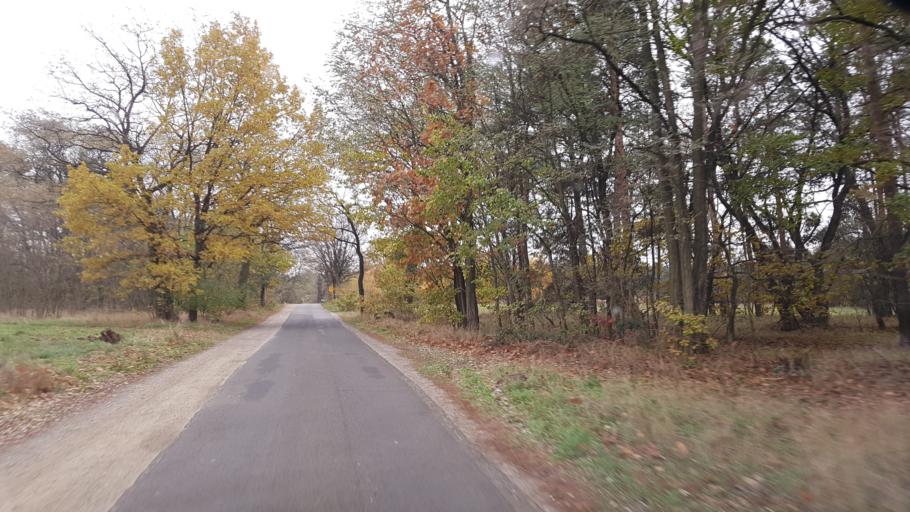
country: DE
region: Brandenburg
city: Crinitz
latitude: 51.7154
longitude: 13.7835
